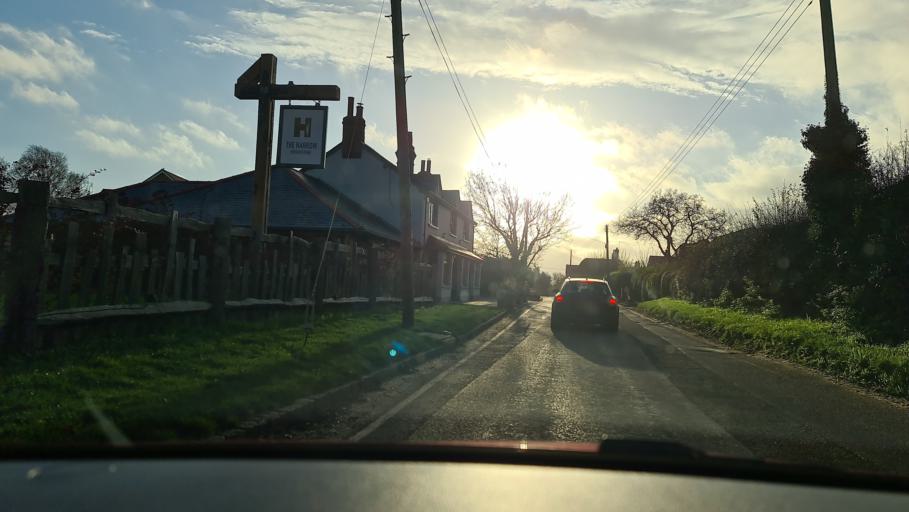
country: GB
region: England
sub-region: Buckinghamshire
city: Stone
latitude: 51.7878
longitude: -0.8385
